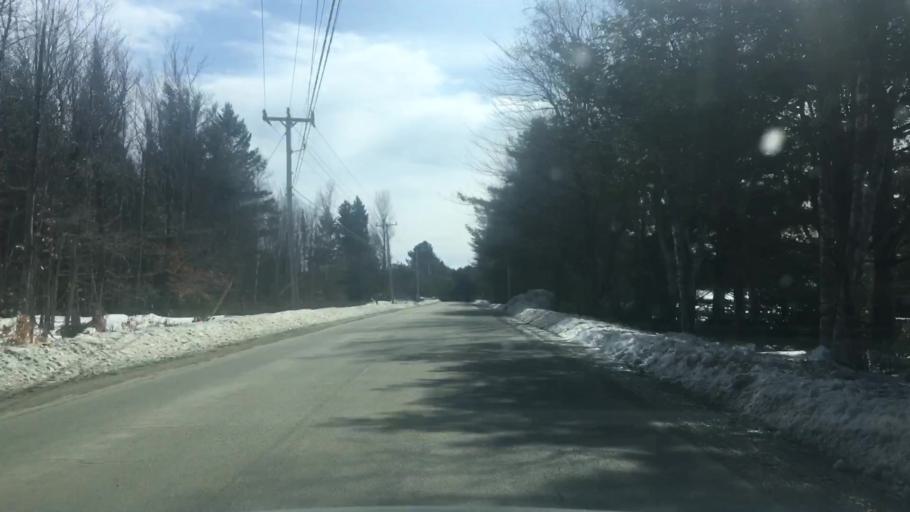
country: US
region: Maine
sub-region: Penobscot County
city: Holden
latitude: 44.7695
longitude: -68.6483
